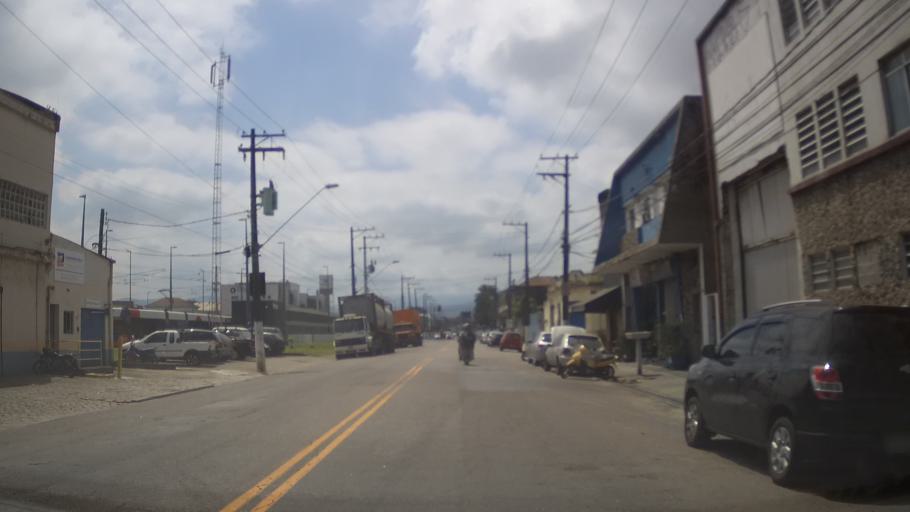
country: BR
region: Sao Paulo
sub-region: Santos
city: Santos
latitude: -23.9579
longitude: -46.3135
